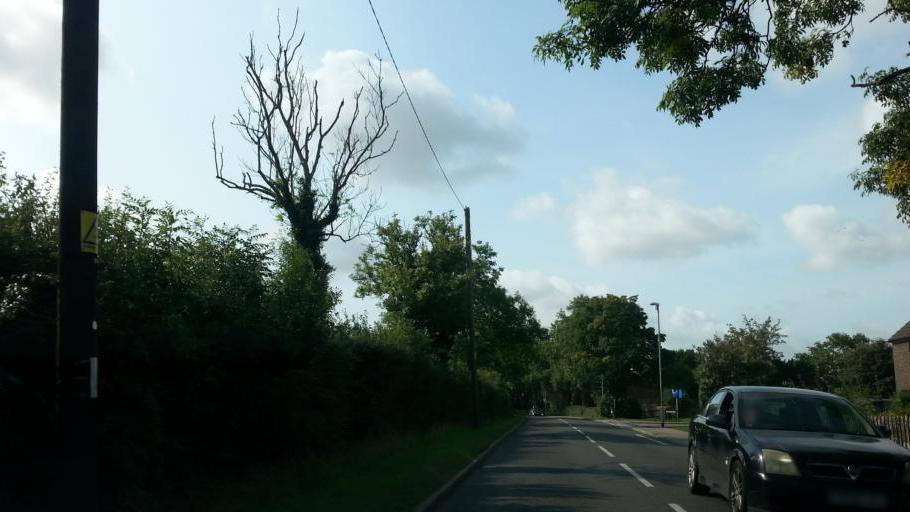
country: GB
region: England
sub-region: Cambridgeshire
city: Comberton
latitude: 52.2151
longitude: 0.0125
